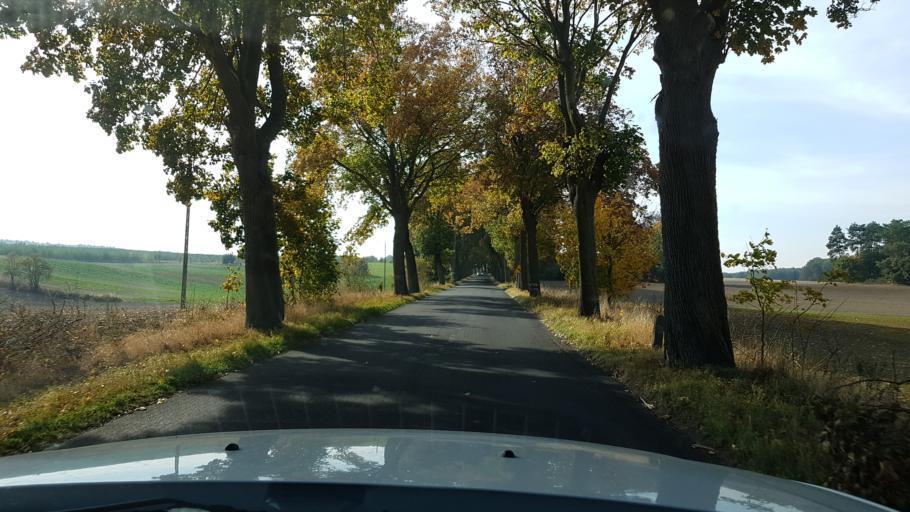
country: PL
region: West Pomeranian Voivodeship
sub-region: Powiat mysliborski
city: Nowogrodek Pomorski
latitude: 52.9501
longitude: 15.0991
